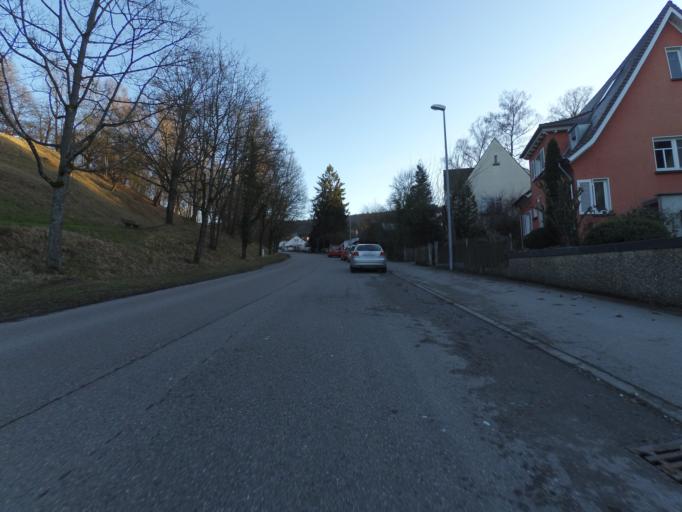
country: DE
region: Baden-Wuerttemberg
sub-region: Regierungsbezirk Stuttgart
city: Aalen
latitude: 48.8284
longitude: 10.0967
